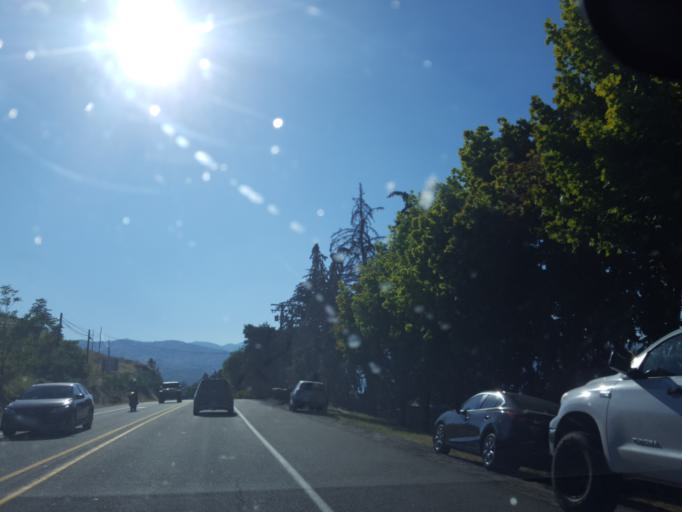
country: US
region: Washington
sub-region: Chelan County
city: Chelan
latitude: 47.8363
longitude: -120.0281
